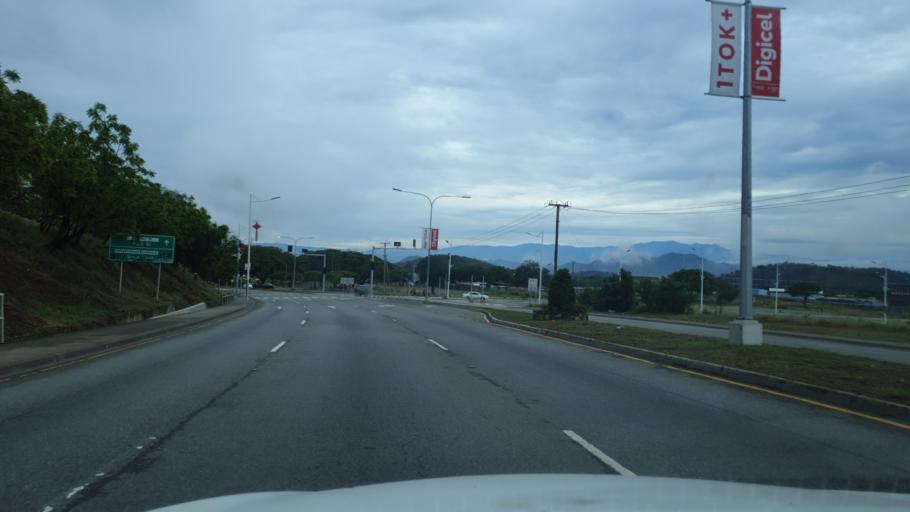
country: PG
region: National Capital
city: Port Moresby
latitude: -9.4292
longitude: 147.1797
